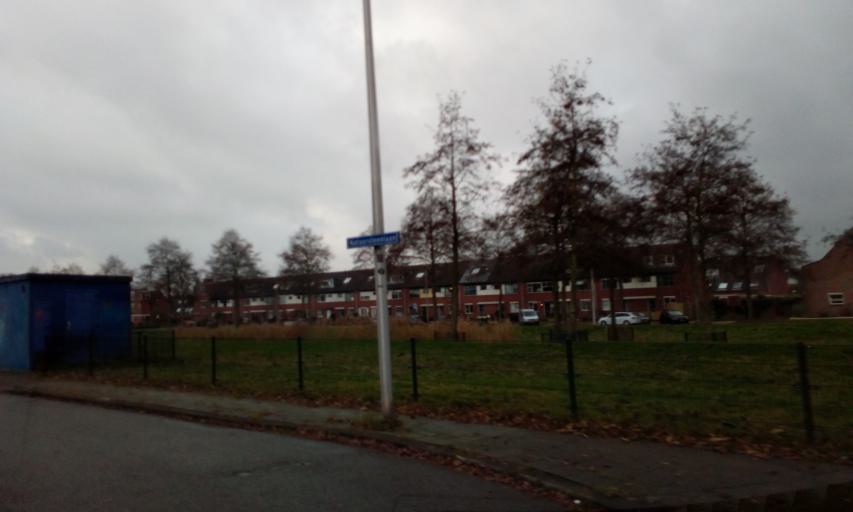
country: NL
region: South Holland
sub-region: Gemeente Zoetermeer
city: Zoetermeer
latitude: 52.0359
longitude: 4.4827
